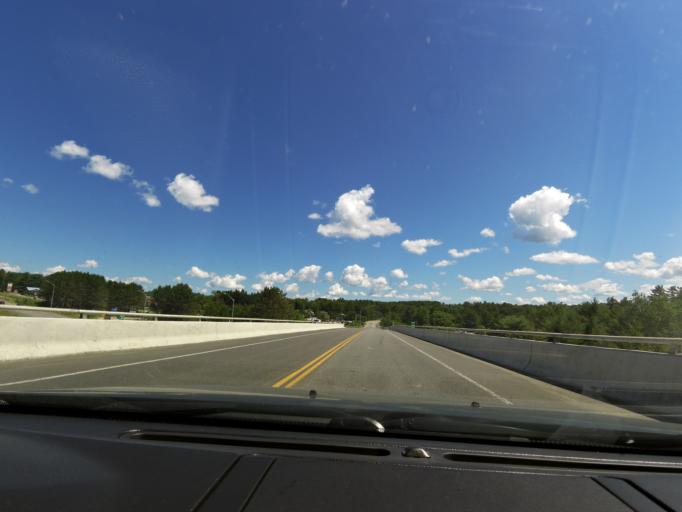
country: CA
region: Ontario
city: Bracebridge
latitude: 45.0525
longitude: -79.2897
